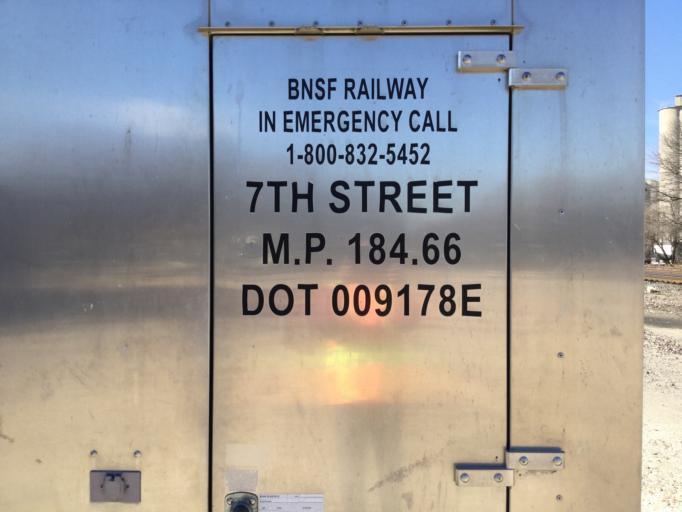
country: US
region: Kansas
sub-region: Harvey County
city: Newton
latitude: 38.0509
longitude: -97.3371
